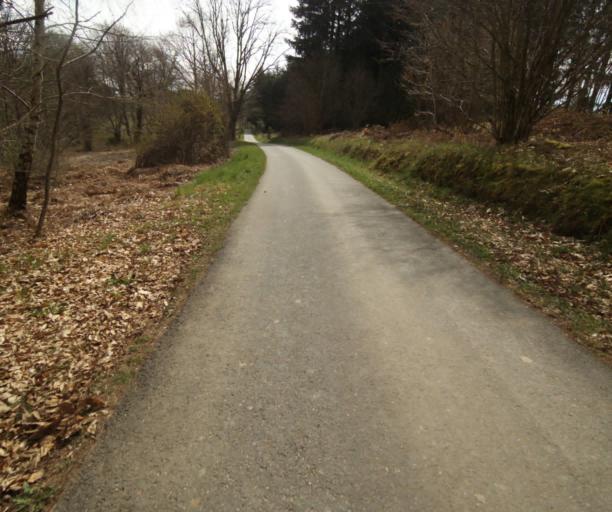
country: FR
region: Limousin
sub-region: Departement de la Correze
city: Egletons
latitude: 45.3623
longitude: 1.9749
